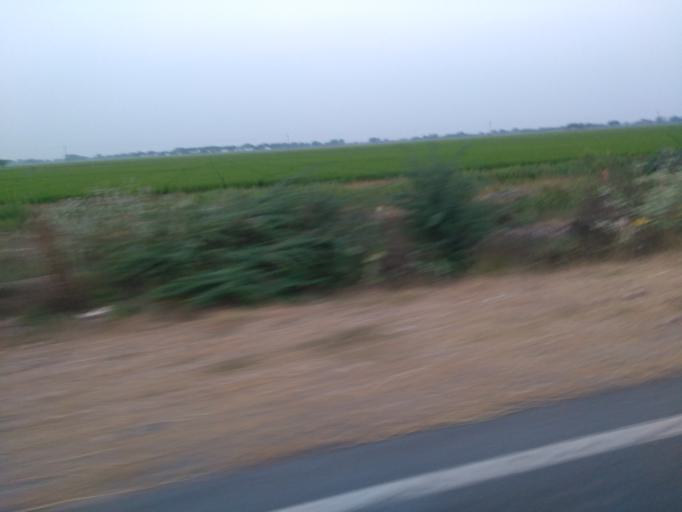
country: IN
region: Andhra Pradesh
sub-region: Cuddapah
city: Proddatur
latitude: 14.7288
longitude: 78.6351
